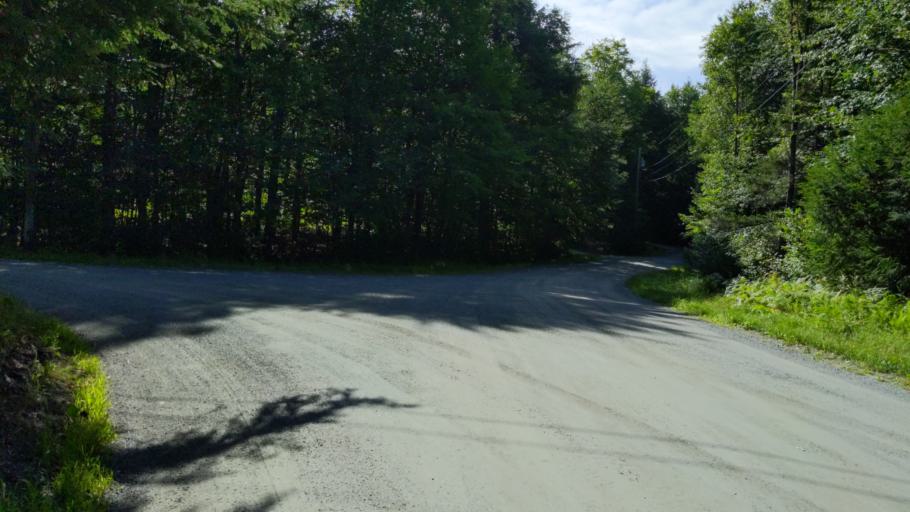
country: US
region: New Hampshire
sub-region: Sullivan County
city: Grantham
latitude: 43.5083
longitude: -72.0972
